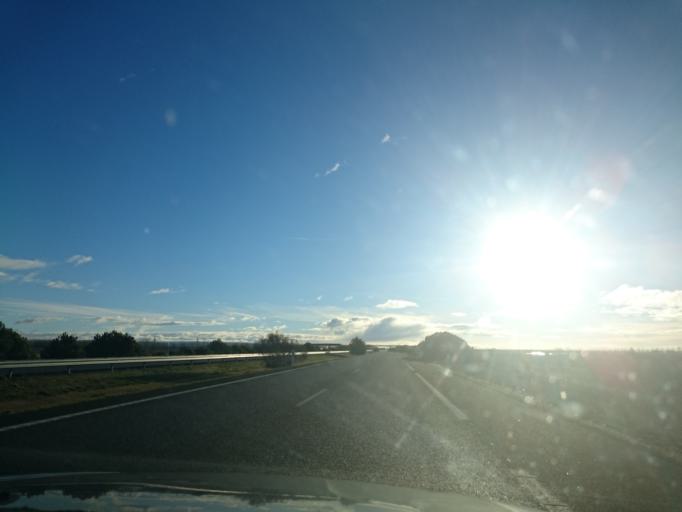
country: ES
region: Castille and Leon
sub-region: Provincia de Leon
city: Bercianos del Real Camino
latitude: 42.4064
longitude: -5.1812
